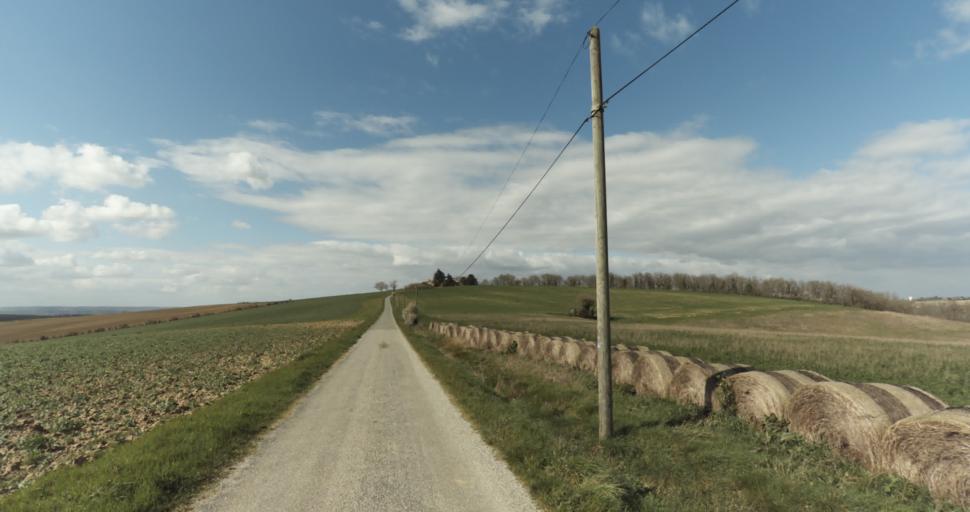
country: FR
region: Midi-Pyrenees
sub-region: Departement de la Haute-Garonne
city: Auterive
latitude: 43.3729
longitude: 1.5049
